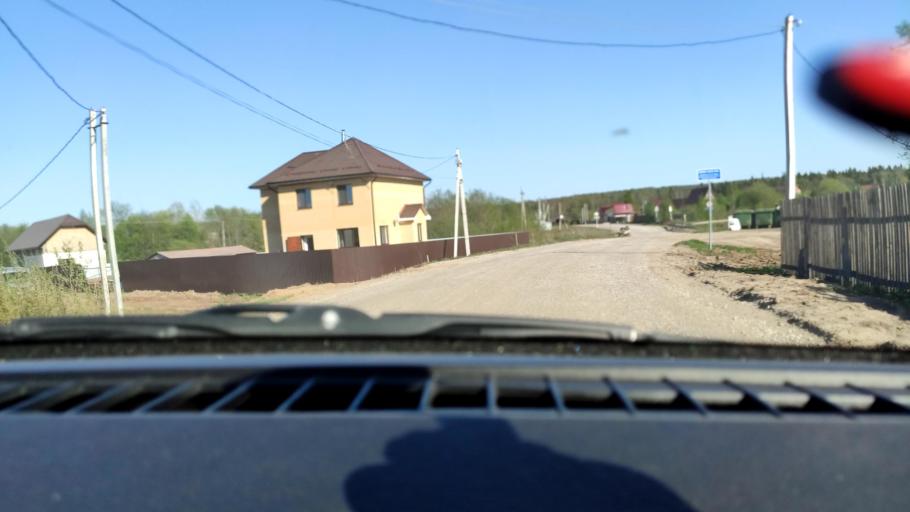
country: RU
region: Perm
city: Overyata
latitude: 58.0788
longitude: 55.9756
